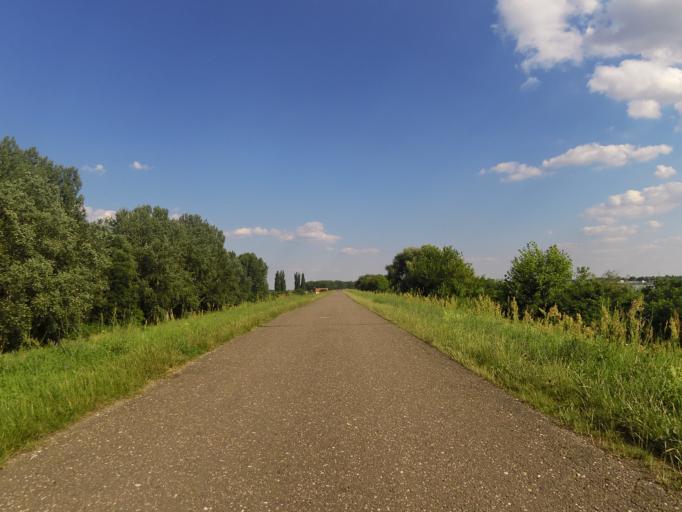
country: HU
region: Jasz-Nagykun-Szolnok
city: Abadszalok
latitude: 47.5007
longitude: 20.6014
